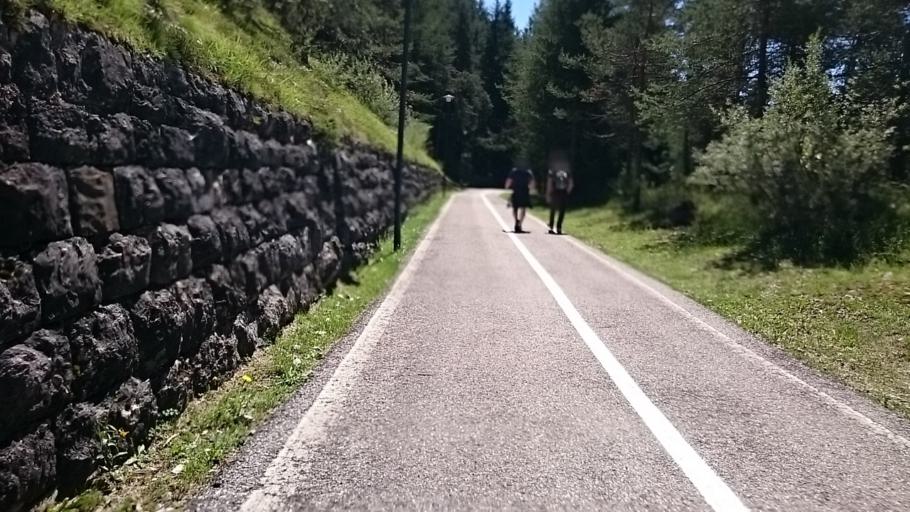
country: IT
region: Veneto
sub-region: Provincia di Belluno
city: San Vito
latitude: 46.4713
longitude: 12.2058
